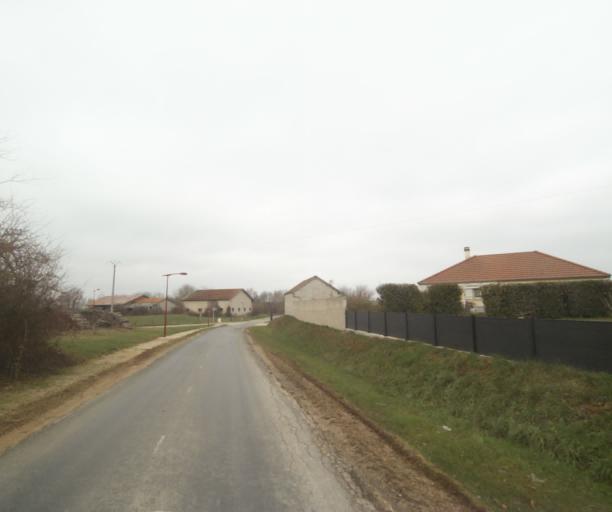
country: FR
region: Champagne-Ardenne
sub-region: Departement de la Marne
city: Pargny-sur-Saulx
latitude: 48.6911
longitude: 4.8058
